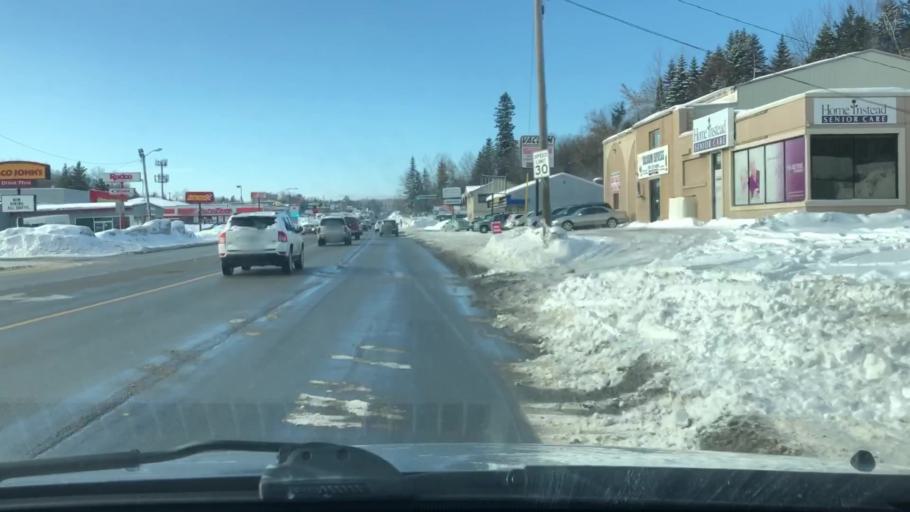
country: US
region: Minnesota
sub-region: Saint Louis County
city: Duluth
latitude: 46.8004
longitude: -92.1247
